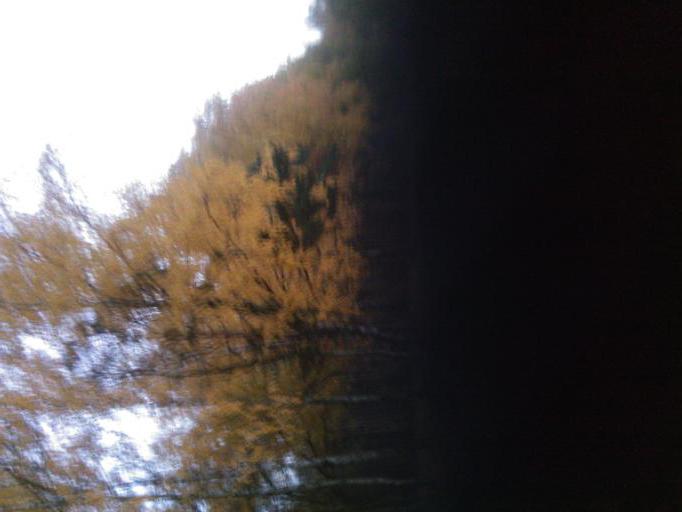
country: RU
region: Moscow
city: Zyuzino
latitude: 55.6363
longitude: 37.5624
